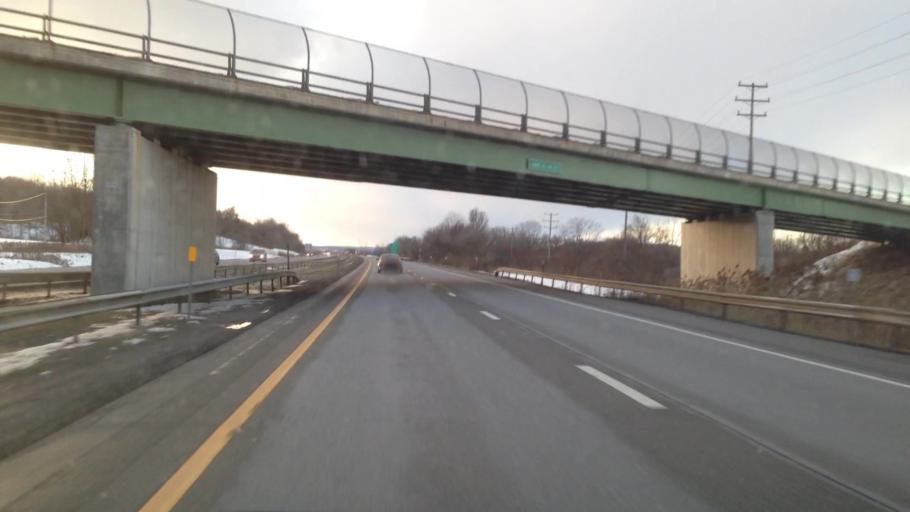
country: US
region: New York
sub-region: Herkimer County
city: Herkimer
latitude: 43.0146
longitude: -74.9473
